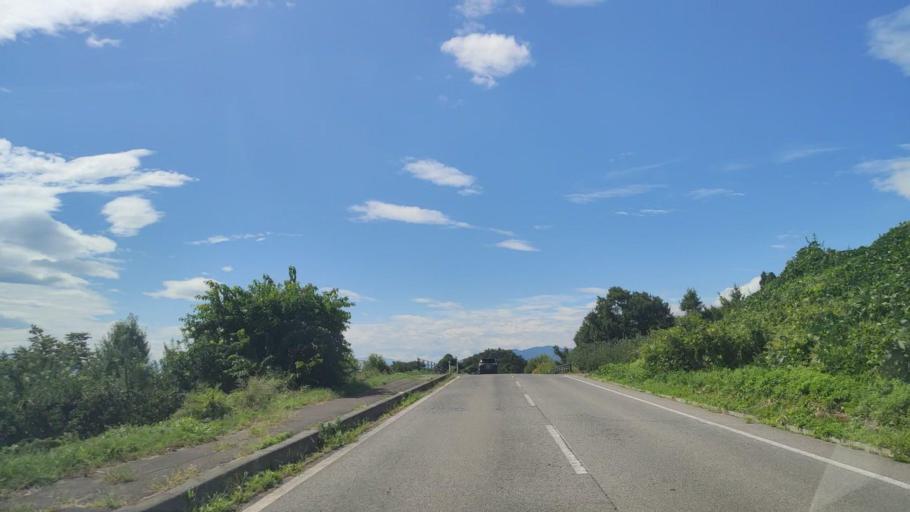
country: JP
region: Nagano
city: Suzaka
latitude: 36.7206
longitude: 138.2855
